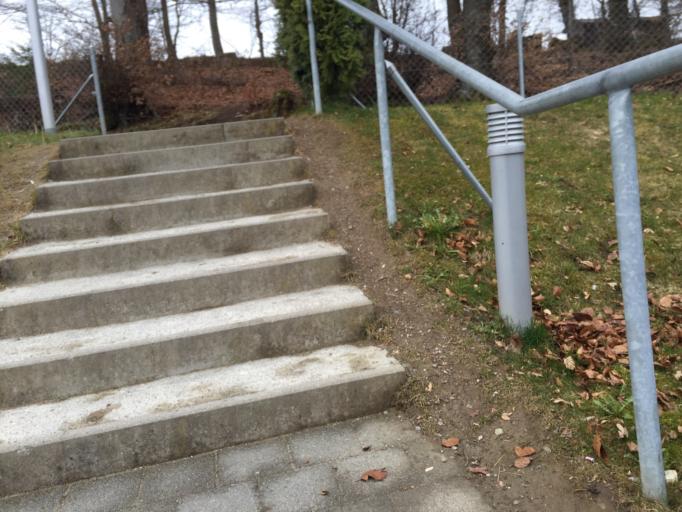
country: CH
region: Bern
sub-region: Bern-Mittelland District
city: Koniz
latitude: 46.9098
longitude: 7.4100
